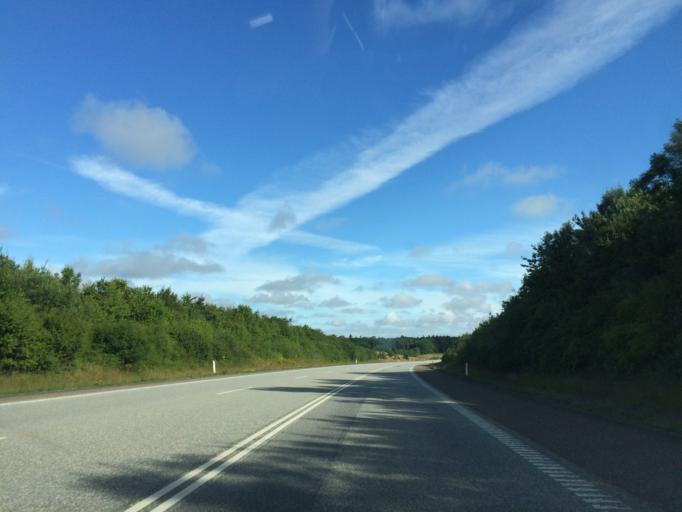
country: DK
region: Central Jutland
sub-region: Silkeborg Kommune
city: Kjellerup
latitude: 56.3408
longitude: 9.5345
